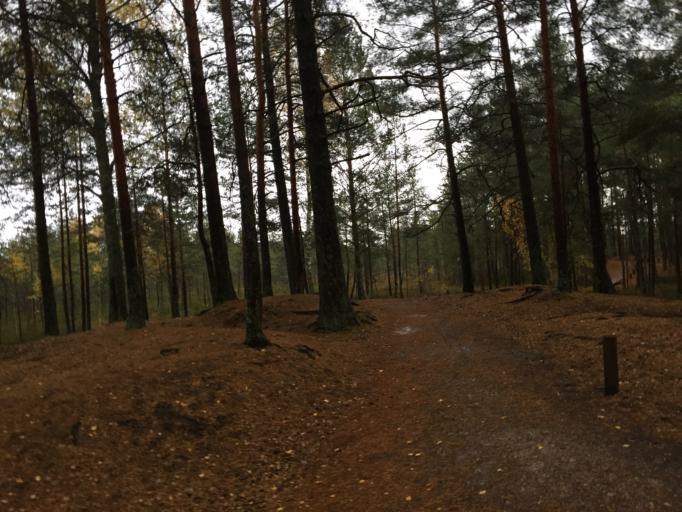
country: LV
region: Engure
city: Smarde
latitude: 56.9105
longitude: 23.4601
